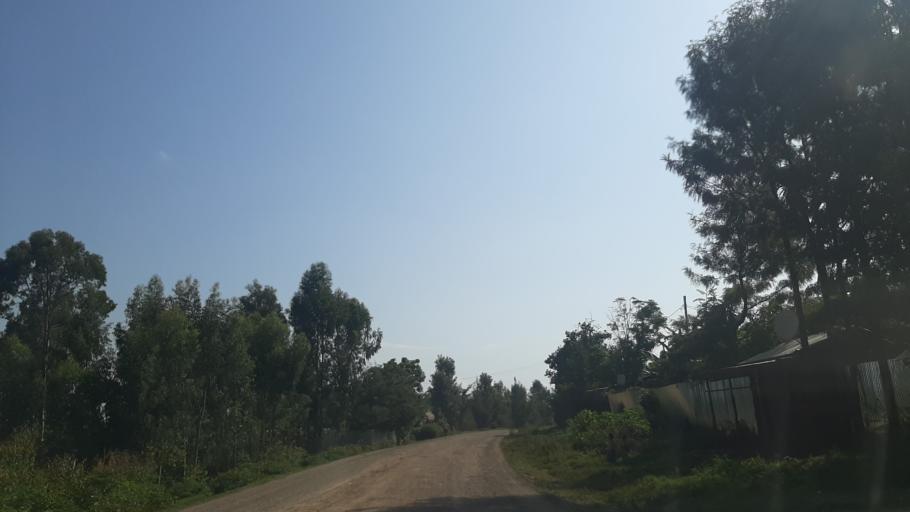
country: ET
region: Oromiya
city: Jima
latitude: 7.7748
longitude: 36.8006
